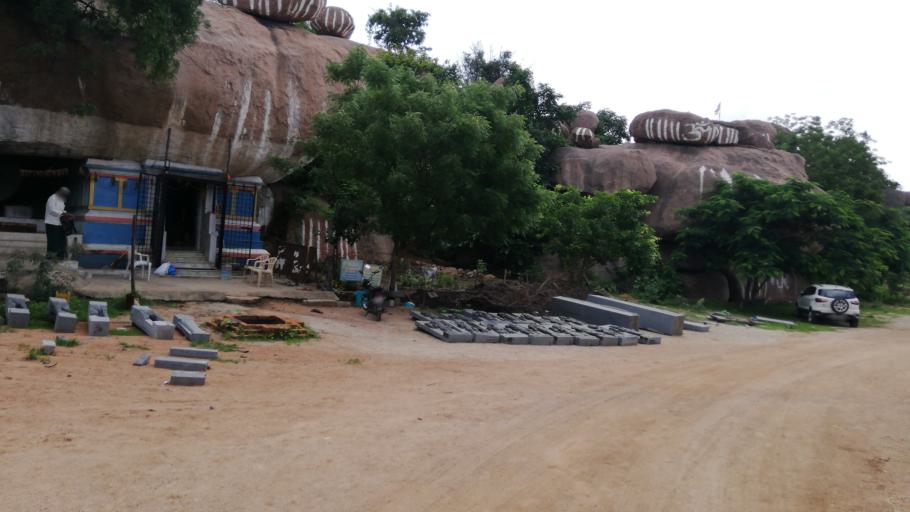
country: IN
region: Telangana
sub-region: Rangareddi
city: Kukatpalli
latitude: 17.4097
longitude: 78.3630
